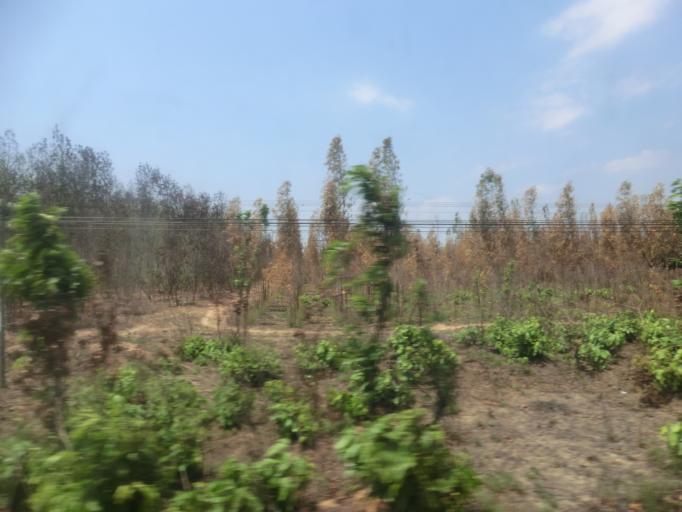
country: VN
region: Binh Thuan
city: Thuan Nam
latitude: 10.9295
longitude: 107.9342
